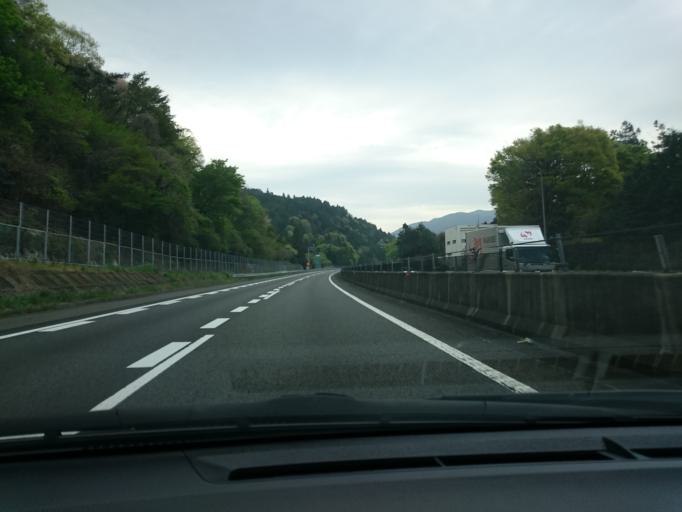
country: JP
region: Gifu
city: Tarui
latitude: 35.3512
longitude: 136.4843
